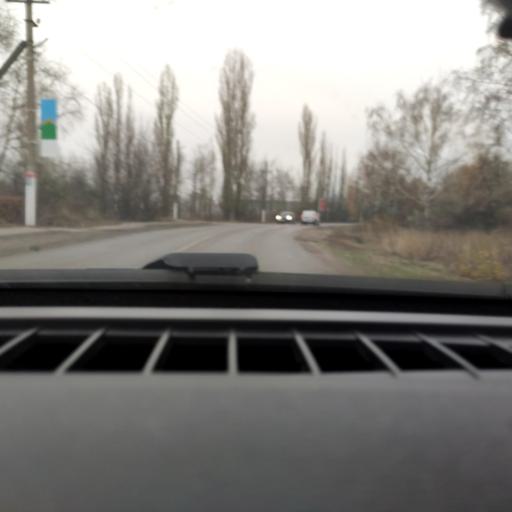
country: RU
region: Voronezj
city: Novaya Usman'
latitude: 51.6574
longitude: 39.3285
